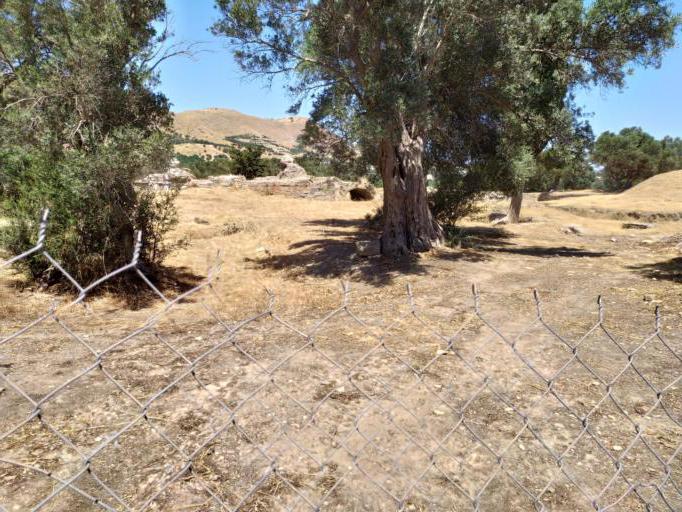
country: GR
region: Crete
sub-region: Nomos Irakleiou
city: Agioi Deka
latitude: 35.0585
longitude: 24.9509
